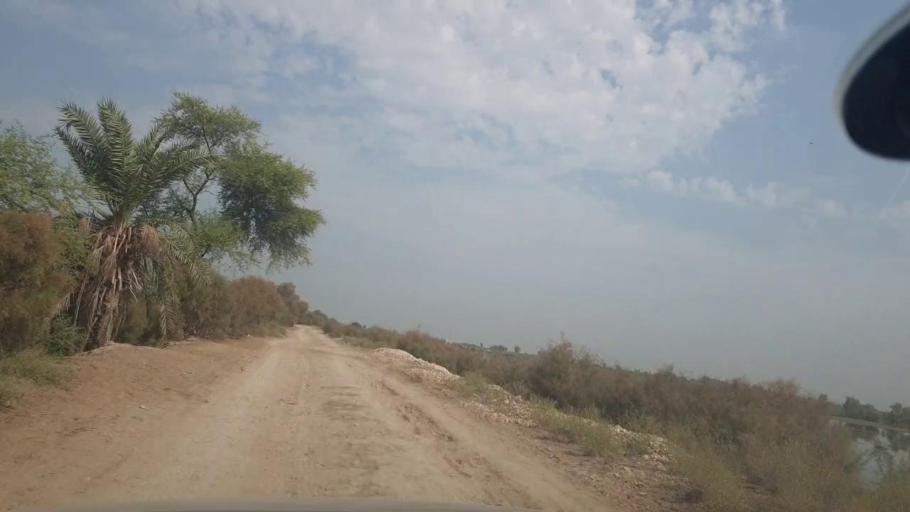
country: PK
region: Balochistan
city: Mehrabpur
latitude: 28.1075
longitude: 68.0910
